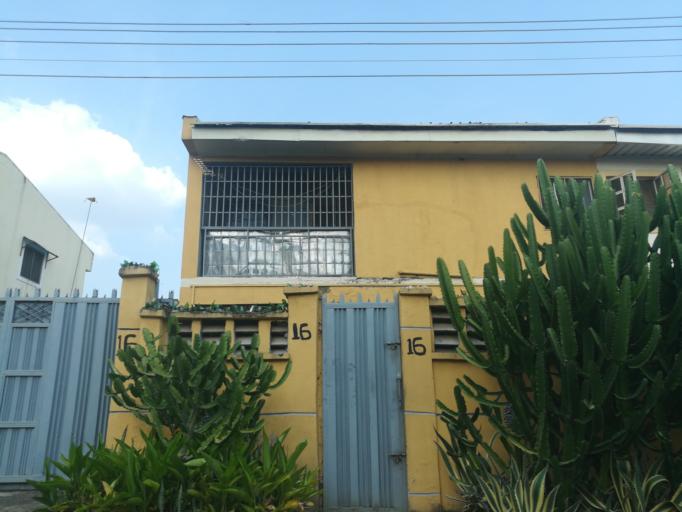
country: NG
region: Abuja Federal Capital Territory
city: Abuja
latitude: 9.0784
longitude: 7.4127
